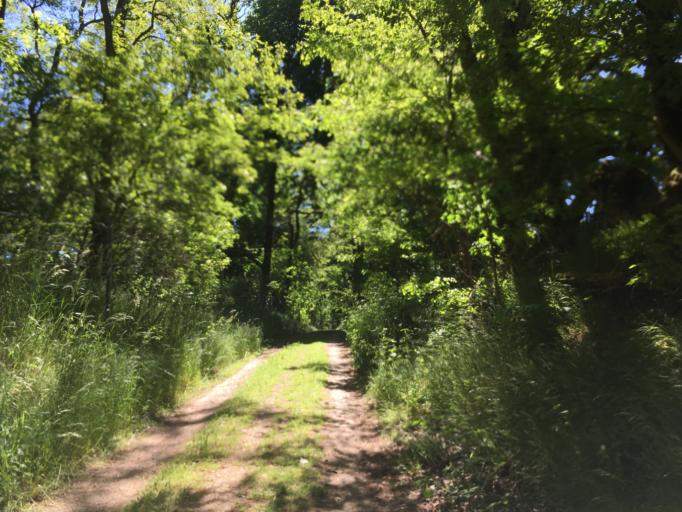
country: DE
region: Brandenburg
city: Zehdenick
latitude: 52.9038
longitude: 13.2426
